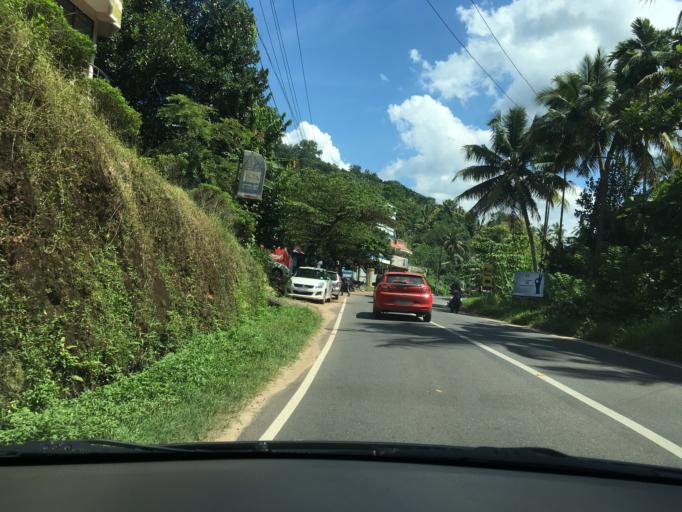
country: IN
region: Kerala
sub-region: Thiruvananthapuram
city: Nedumangad
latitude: 8.5801
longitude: 76.9954
